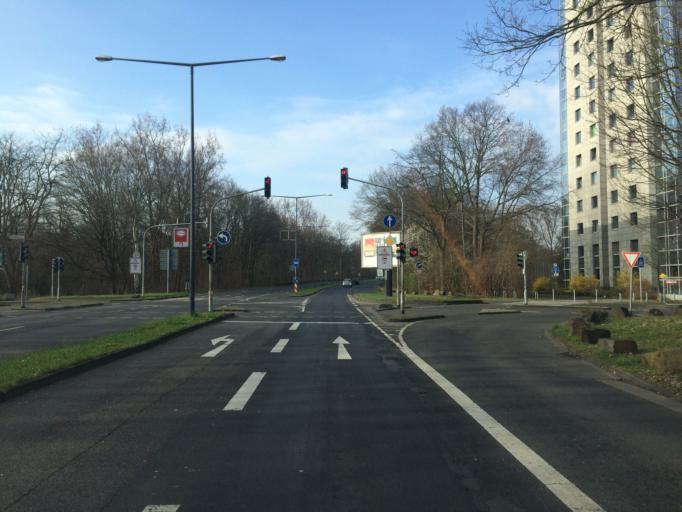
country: DE
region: North Rhine-Westphalia
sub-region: Regierungsbezirk Koln
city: Humboldtkolonie
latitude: 50.9323
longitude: 6.9896
